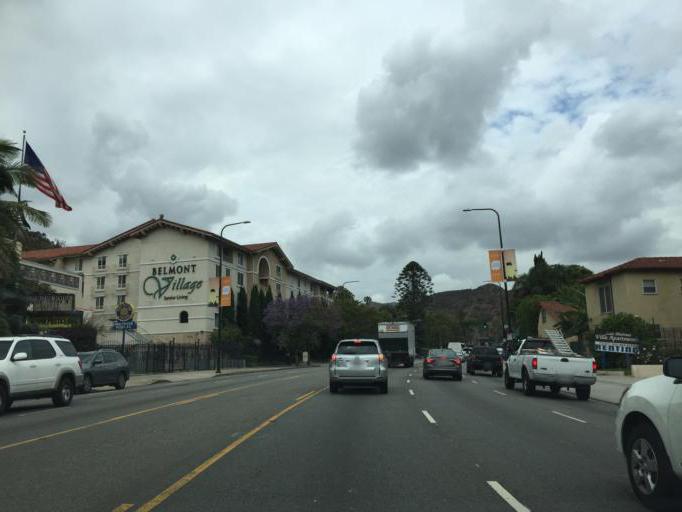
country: US
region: California
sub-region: Los Angeles County
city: Hollywood
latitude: 34.1072
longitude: -118.3375
